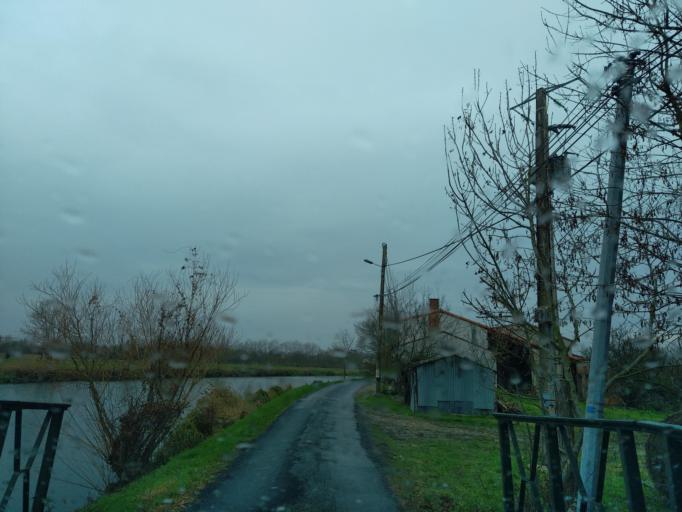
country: FR
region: Pays de la Loire
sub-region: Departement de la Vendee
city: Maillezais
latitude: 46.3185
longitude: -0.7789
